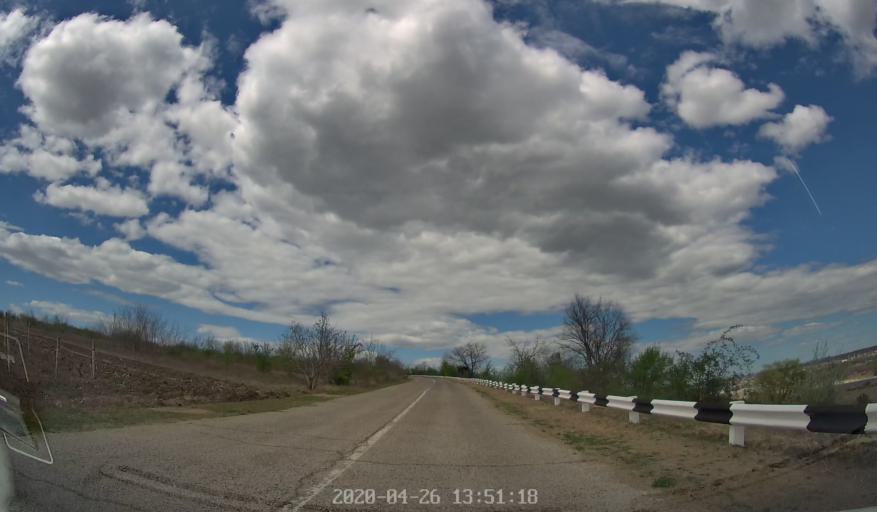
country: MD
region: Telenesti
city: Dubasari
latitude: 47.2662
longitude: 29.1248
